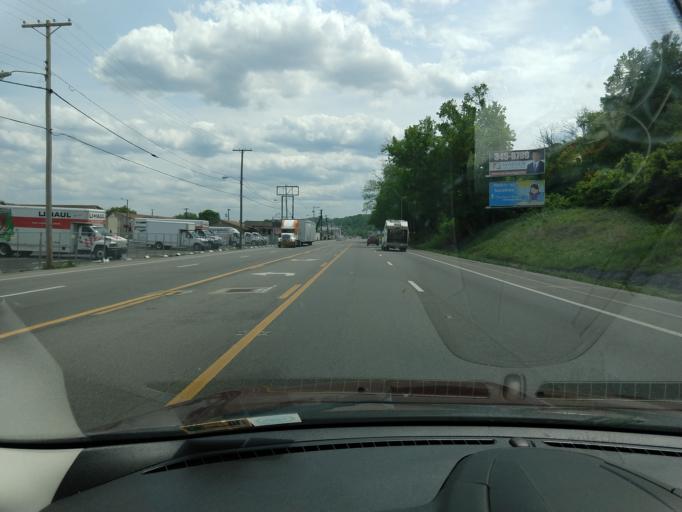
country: US
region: West Virginia
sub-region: Kanawha County
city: Dunbar
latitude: 38.3657
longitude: -81.7635
